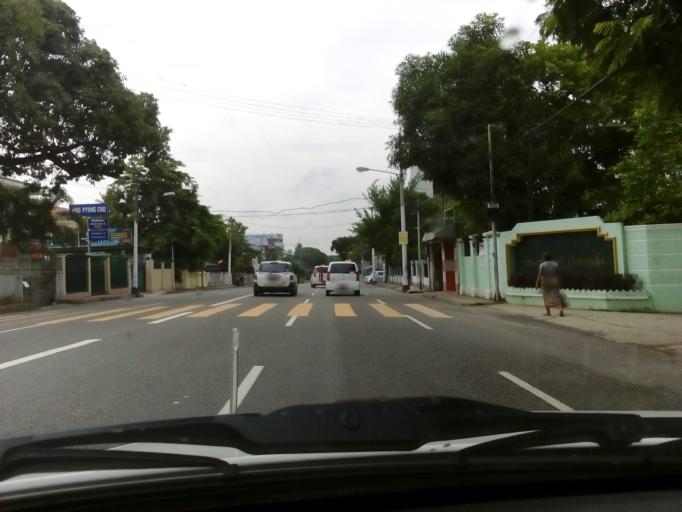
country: MM
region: Yangon
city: Yangon
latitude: 16.8198
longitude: 96.1558
